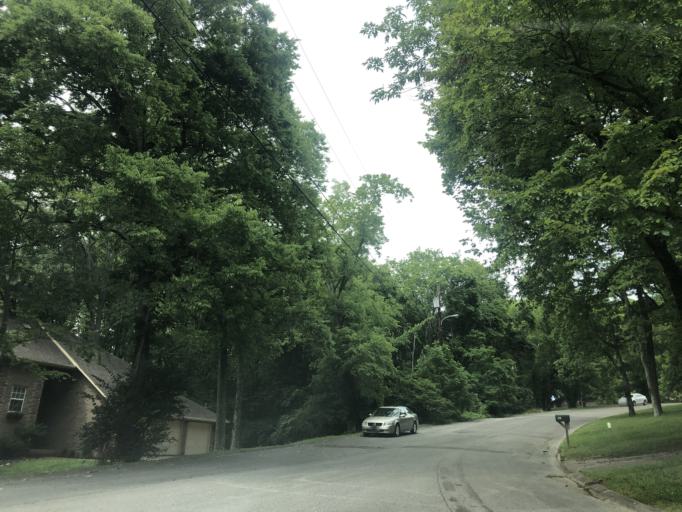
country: US
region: Tennessee
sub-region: Davidson County
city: Nashville
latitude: 36.2097
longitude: -86.8073
